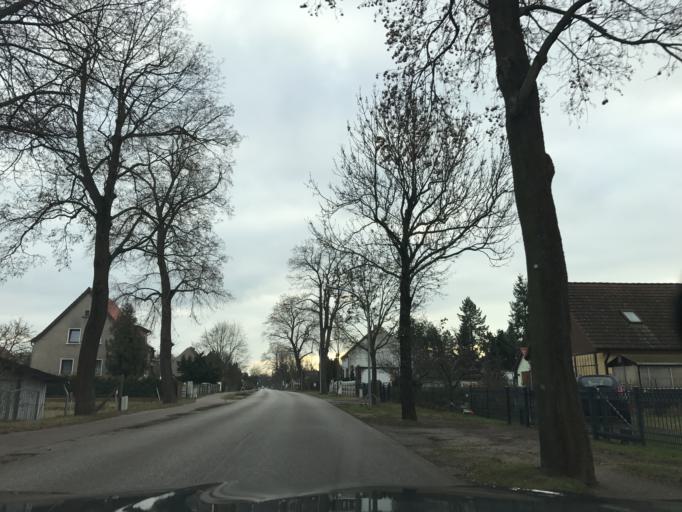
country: DE
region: Brandenburg
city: Brandenburg an der Havel
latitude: 52.3811
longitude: 12.5449
